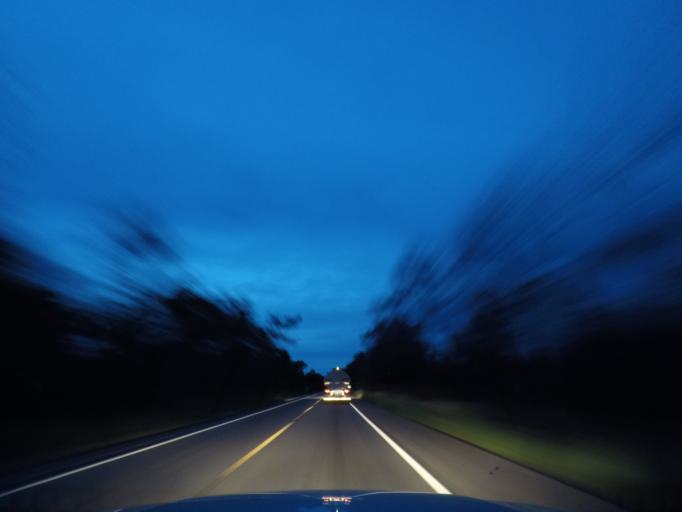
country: BR
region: Bahia
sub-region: Andarai
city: Vera Cruz
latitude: -12.4939
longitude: -41.3360
